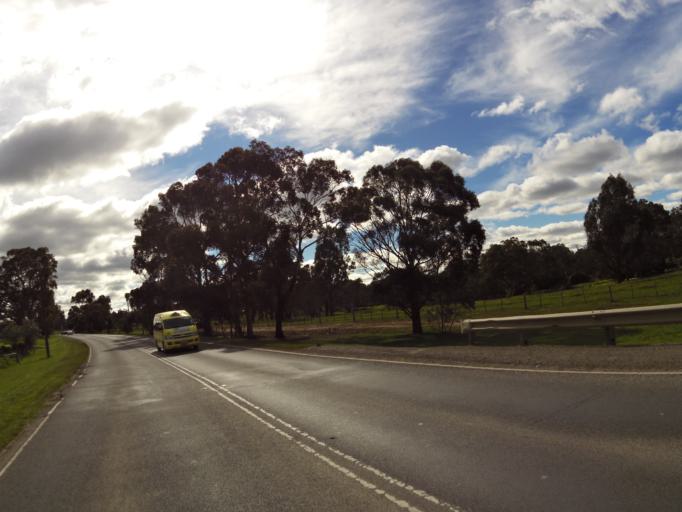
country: AU
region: Victoria
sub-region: Hume
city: Greenvale
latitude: -37.6334
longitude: 144.8355
